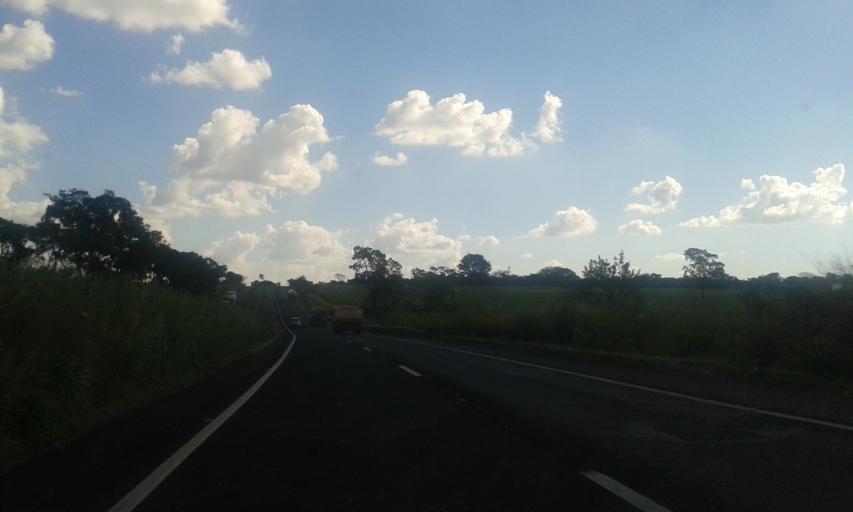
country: BR
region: Minas Gerais
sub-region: Monte Alegre De Minas
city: Monte Alegre de Minas
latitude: -18.8905
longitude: -48.6748
